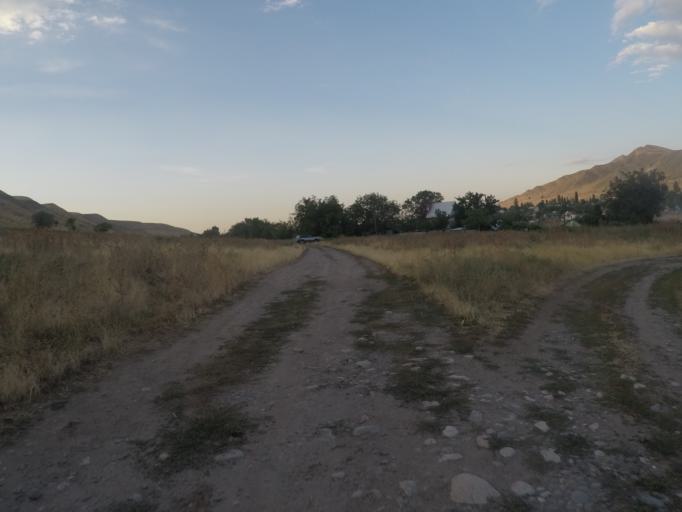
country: KG
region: Chuy
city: Bishkek
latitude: 42.7662
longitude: 74.6382
